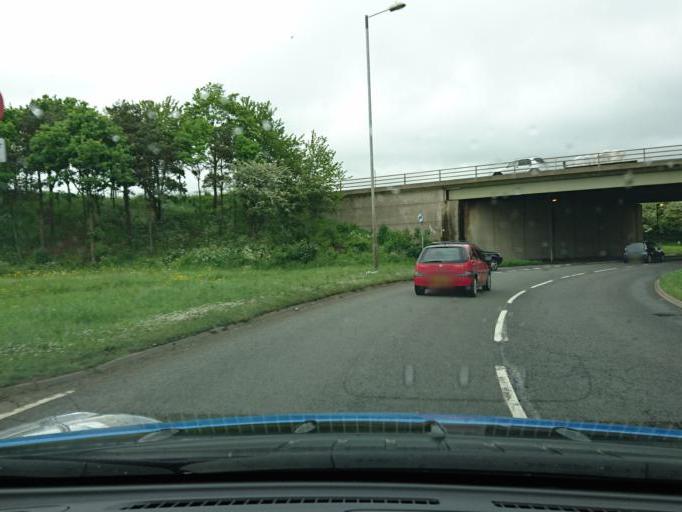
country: GB
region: England
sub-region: Borough of Swindon
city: Wanborough
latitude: 51.5768
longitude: -1.7348
